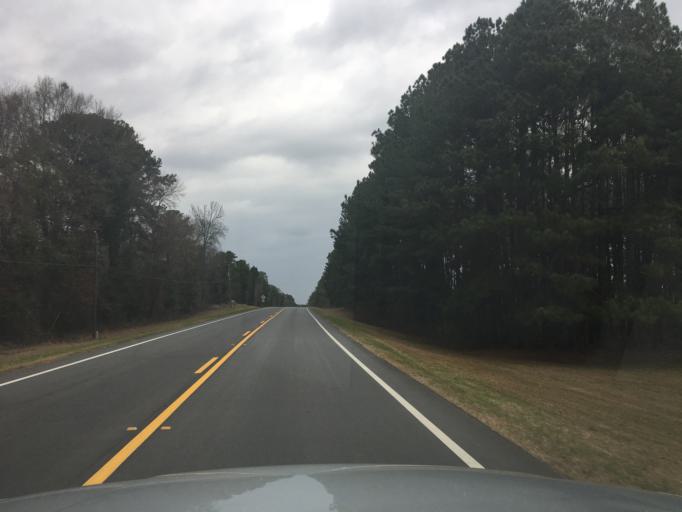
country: US
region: Georgia
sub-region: Columbia County
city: Appling
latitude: 33.6751
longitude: -82.3363
